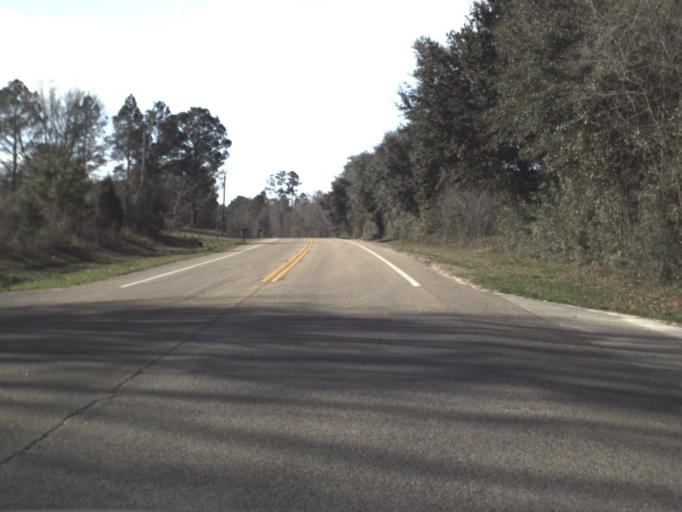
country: US
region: Florida
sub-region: Jackson County
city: Marianna
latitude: 30.6594
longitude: -85.2193
